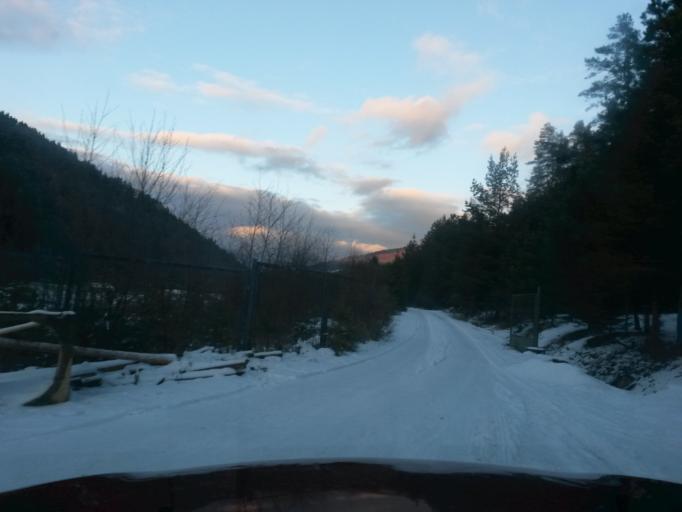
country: SK
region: Kosicky
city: Medzev
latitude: 48.7824
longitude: 20.7964
